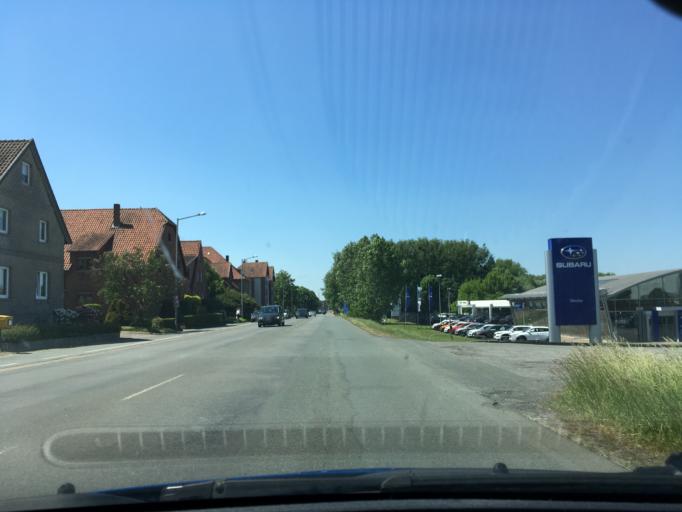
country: DE
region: Lower Saxony
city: Stadthagen
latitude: 52.3288
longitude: 9.2248
